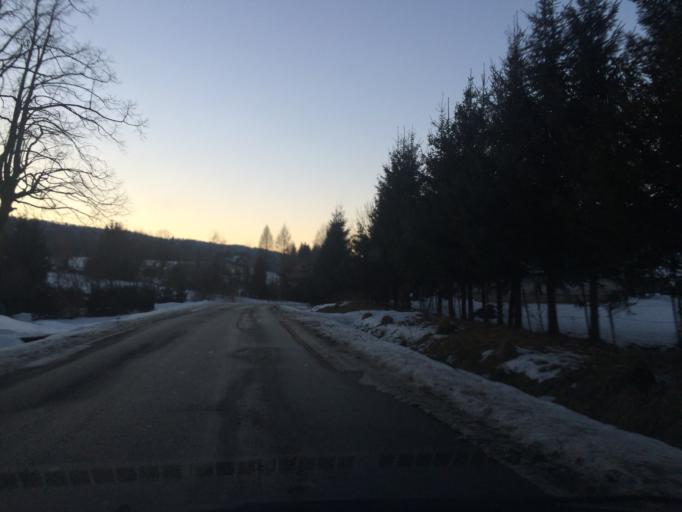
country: PL
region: Subcarpathian Voivodeship
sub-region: Powiat bieszczadzki
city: Ustrzyki Dolne
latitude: 49.4005
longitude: 22.5966
